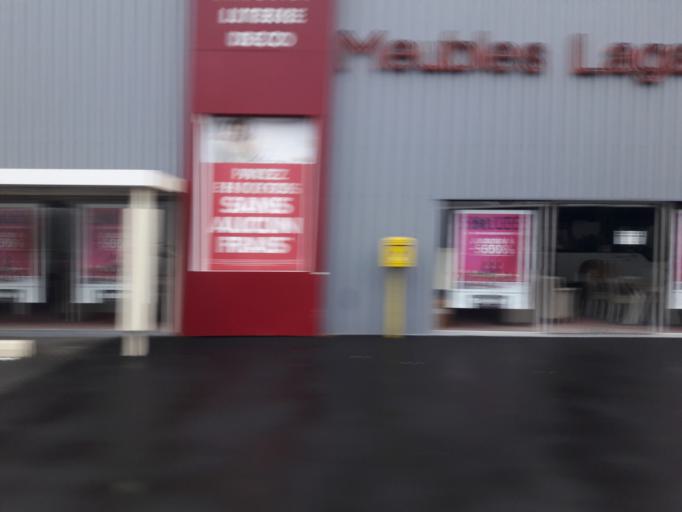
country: FR
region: Ile-de-France
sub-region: Departement de l'Essonne
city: Epinay-sur-Orge
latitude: 48.6757
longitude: 2.3229
